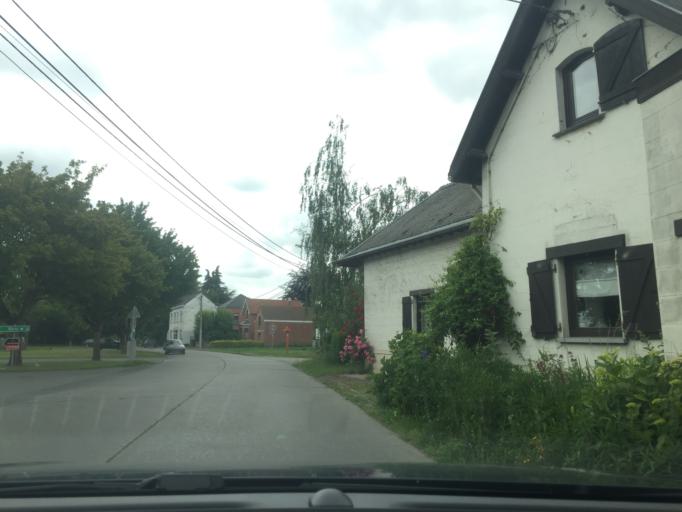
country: BE
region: Wallonia
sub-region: Province du Hainaut
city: Tournai
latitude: 50.6415
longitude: 3.3999
